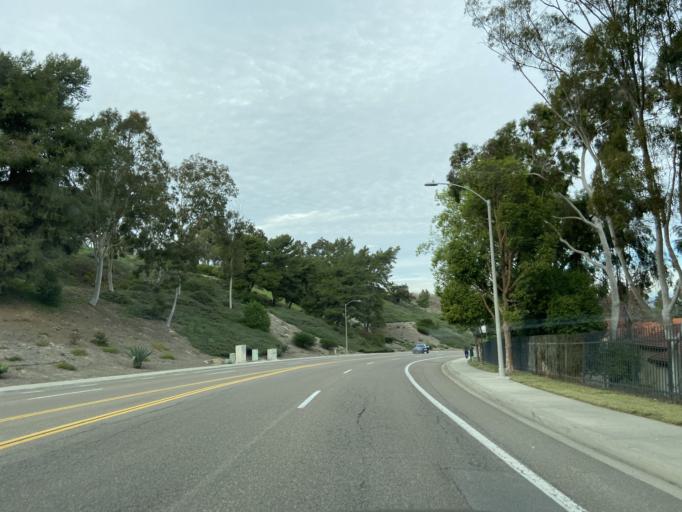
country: US
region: California
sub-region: San Diego County
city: Camp Pendleton South
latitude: 33.2227
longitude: -117.3204
